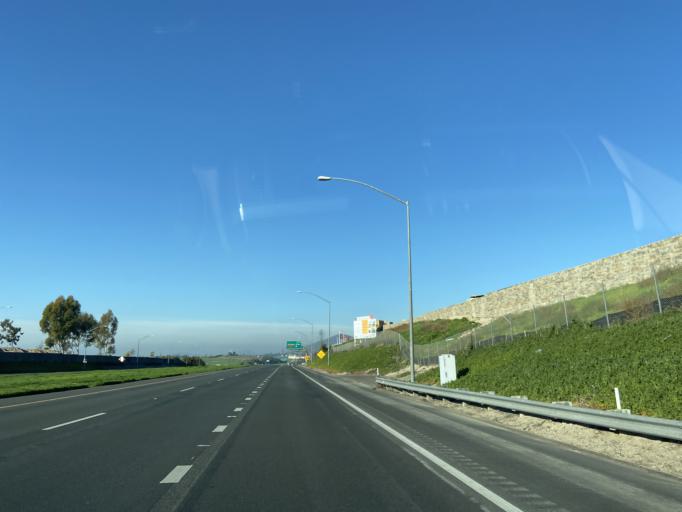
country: US
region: California
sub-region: San Diego County
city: Bonita
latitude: 32.6258
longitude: -116.9711
